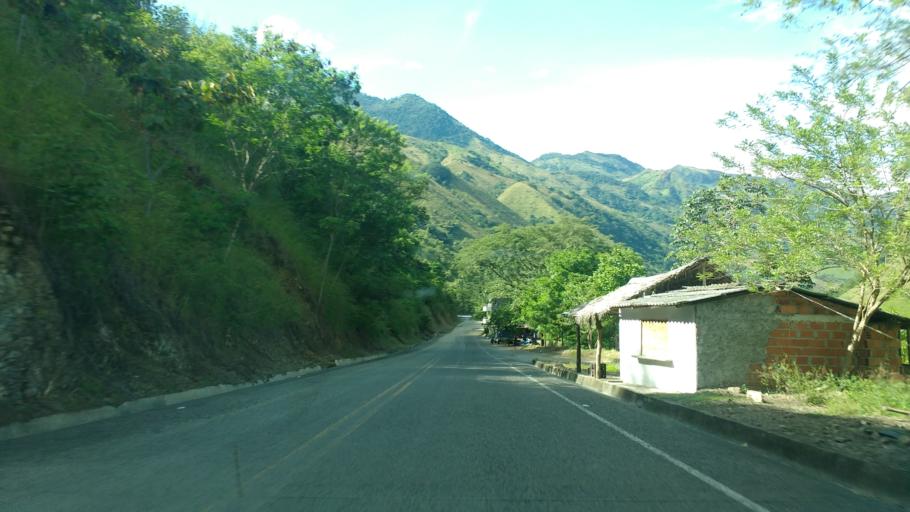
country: CO
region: Antioquia
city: Concordia
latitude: 6.0394
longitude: -75.8607
